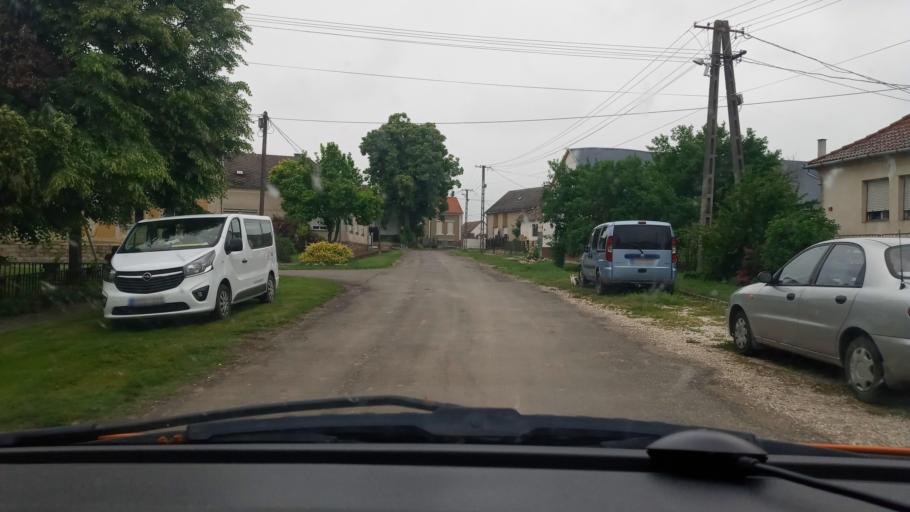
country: HU
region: Baranya
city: Szentlorinc
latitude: 46.0528
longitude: 17.9663
